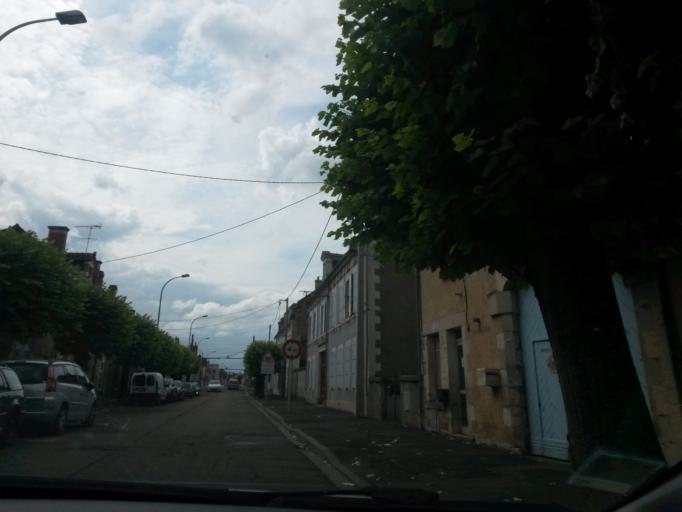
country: FR
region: Bourgogne
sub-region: Departement de la Nievre
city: Cosne-Cours-sur-Loire
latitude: 47.4099
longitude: 2.9332
